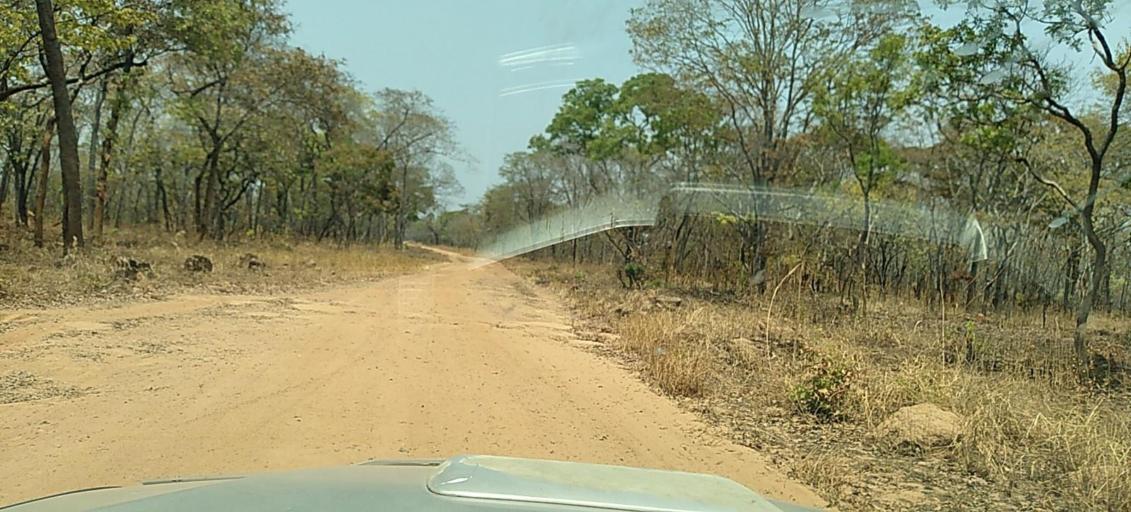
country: ZM
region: North-Western
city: Kasempa
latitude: -13.6116
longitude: 26.1964
